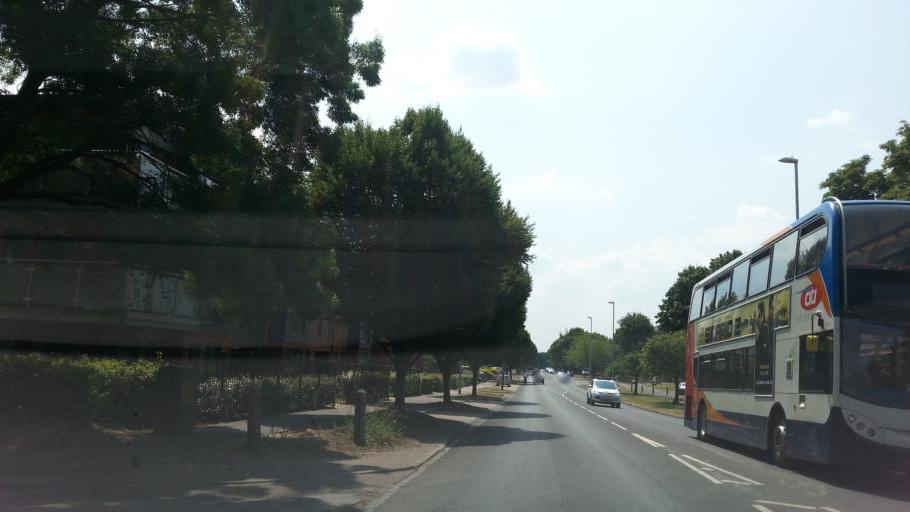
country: GB
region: England
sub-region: Cambridgeshire
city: Cambridge
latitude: 52.2114
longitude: 0.1629
